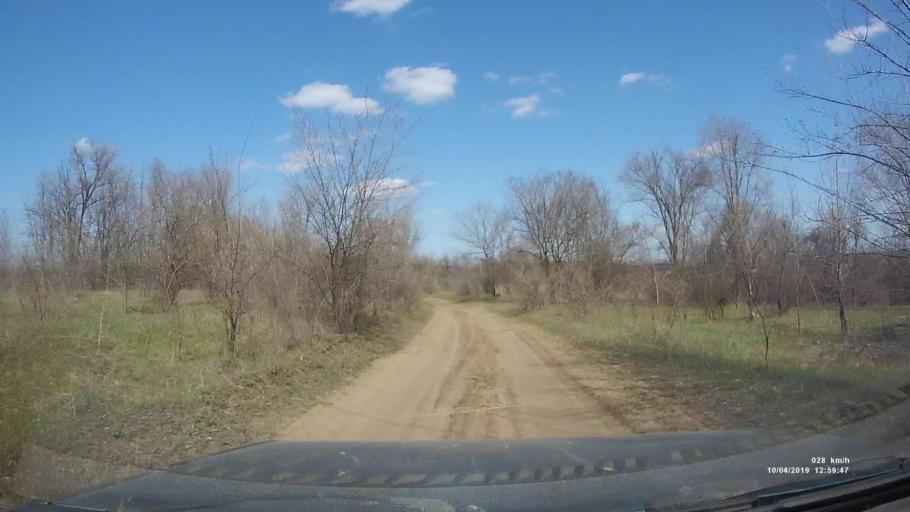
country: RU
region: Rostov
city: Masalovka
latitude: 48.3788
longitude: 40.2289
